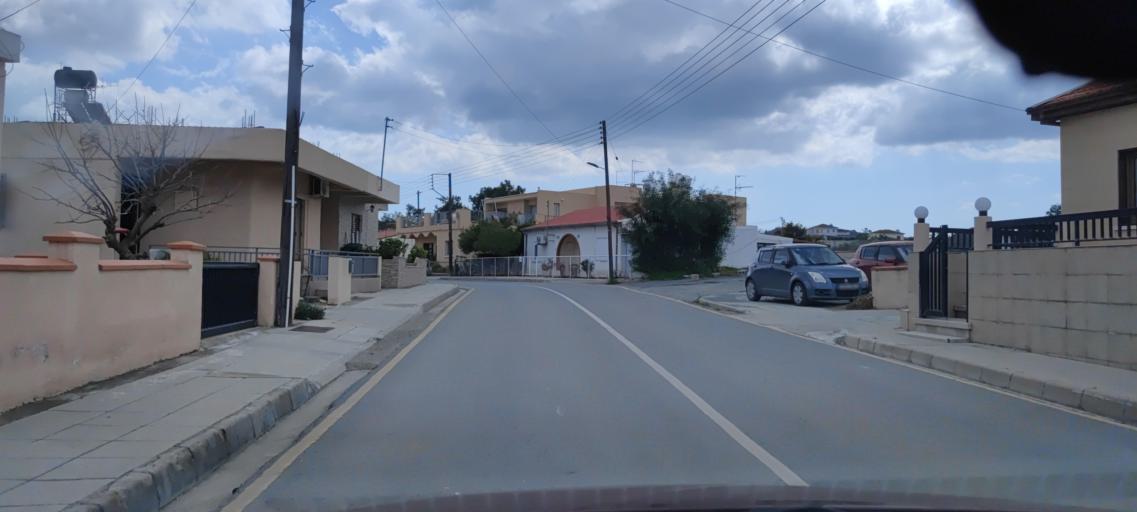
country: CY
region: Larnaka
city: Kornos
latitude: 34.9194
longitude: 33.3991
